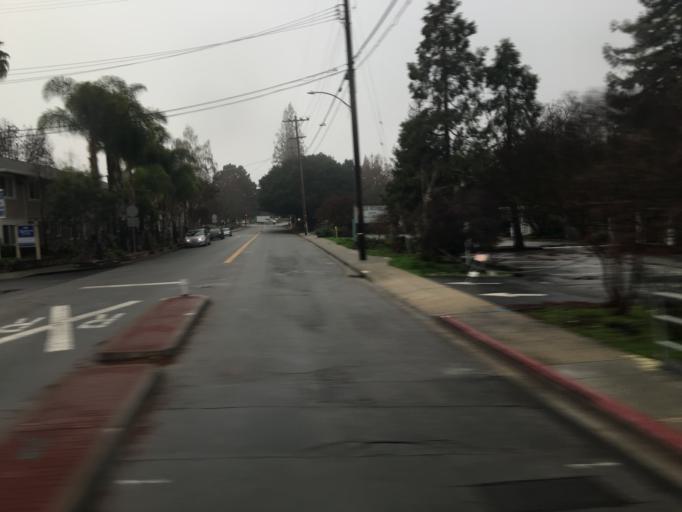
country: US
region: California
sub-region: San Mateo County
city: Atherton
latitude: 37.4594
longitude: -122.1896
